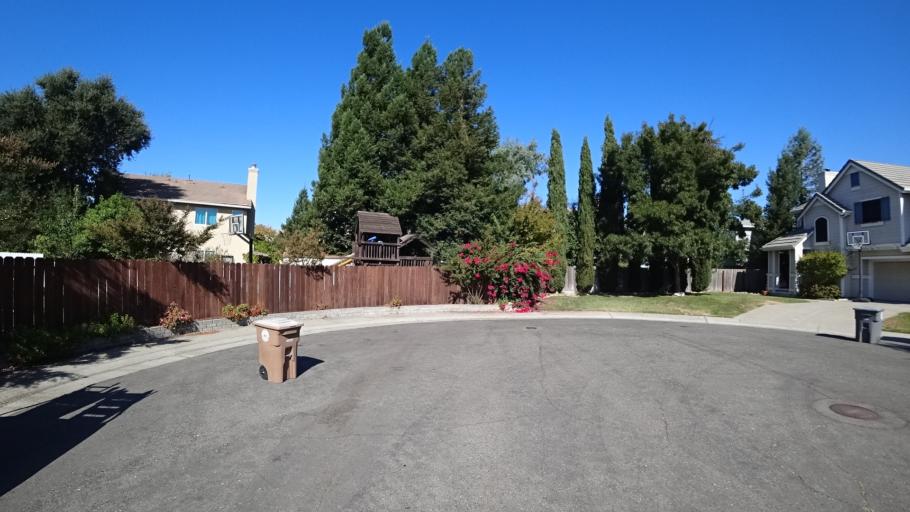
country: US
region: California
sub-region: Sacramento County
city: Laguna
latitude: 38.4367
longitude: -121.4384
